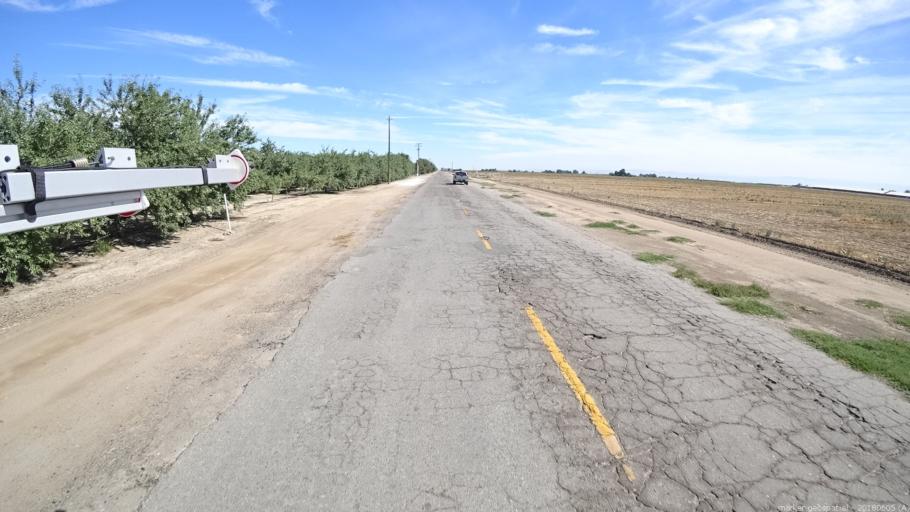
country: US
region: California
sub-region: Madera County
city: Chowchilla
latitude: 37.1043
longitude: -120.4008
